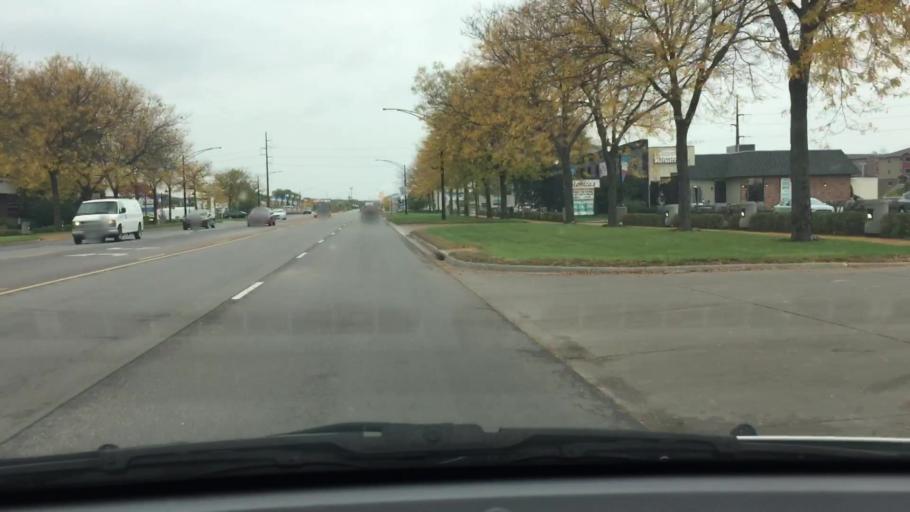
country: US
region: Iowa
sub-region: Johnson County
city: Coralville
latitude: 41.6700
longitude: -91.5684
